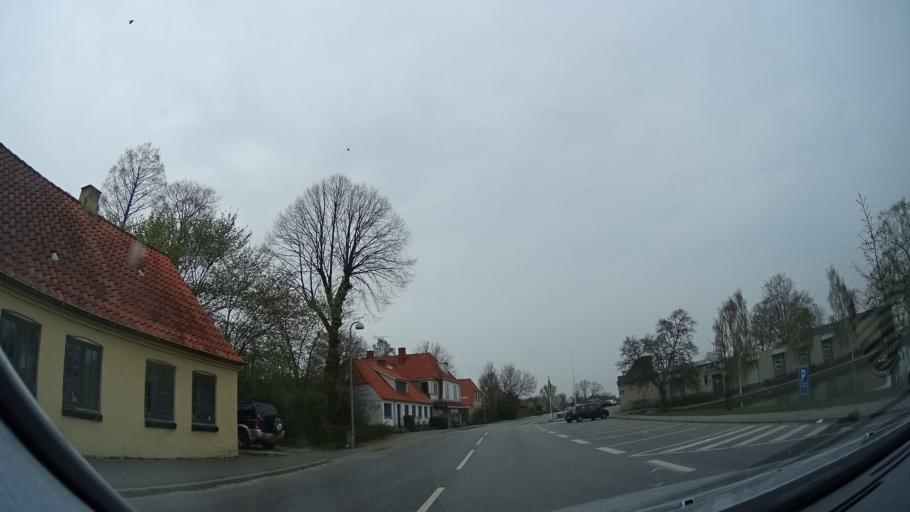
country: DK
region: Zealand
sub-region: Lejre Kommune
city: Ejby
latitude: 55.7072
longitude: 11.9004
